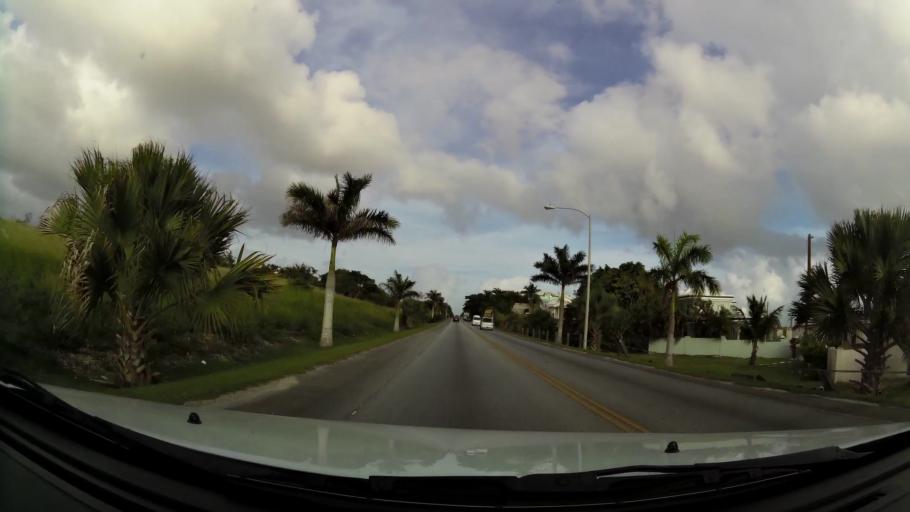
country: BB
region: Christ Church
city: Oistins
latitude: 13.0809
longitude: -59.5479
